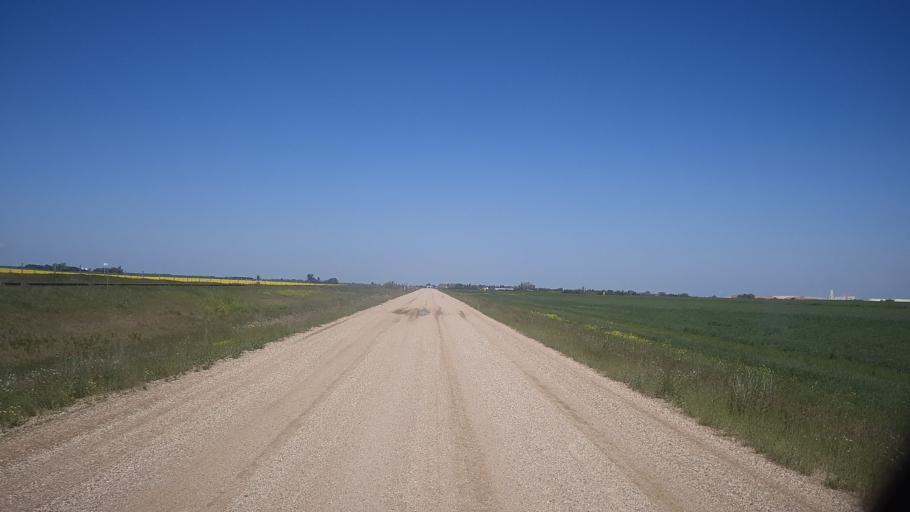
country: CA
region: Saskatchewan
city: Watrous
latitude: 51.8799
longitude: -106.0192
